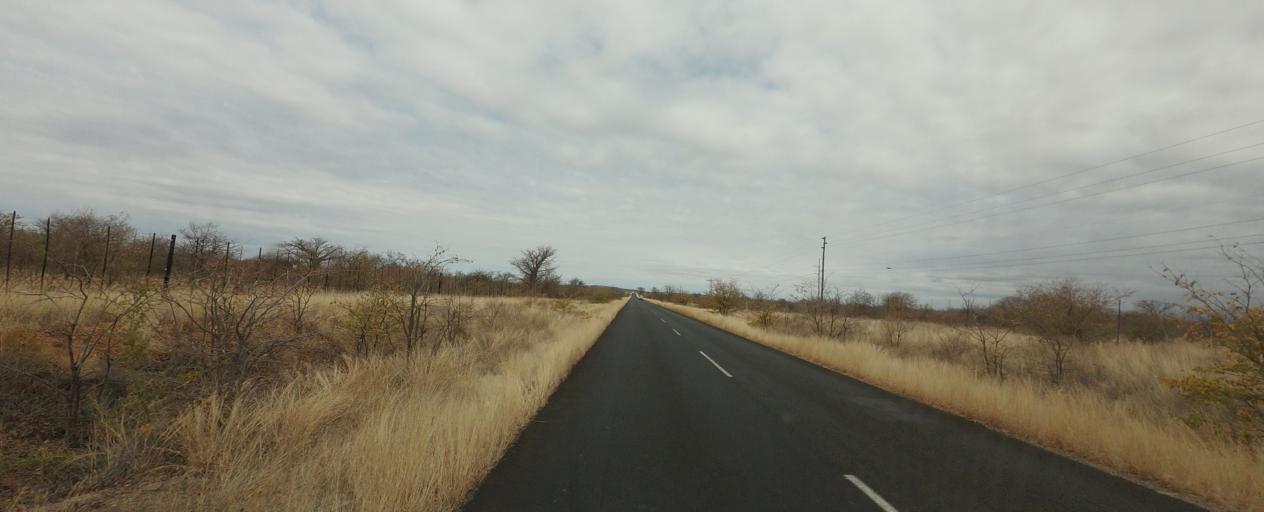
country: ZW
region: Matabeleland South
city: Beitbridge
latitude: -22.4312
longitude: 29.4601
